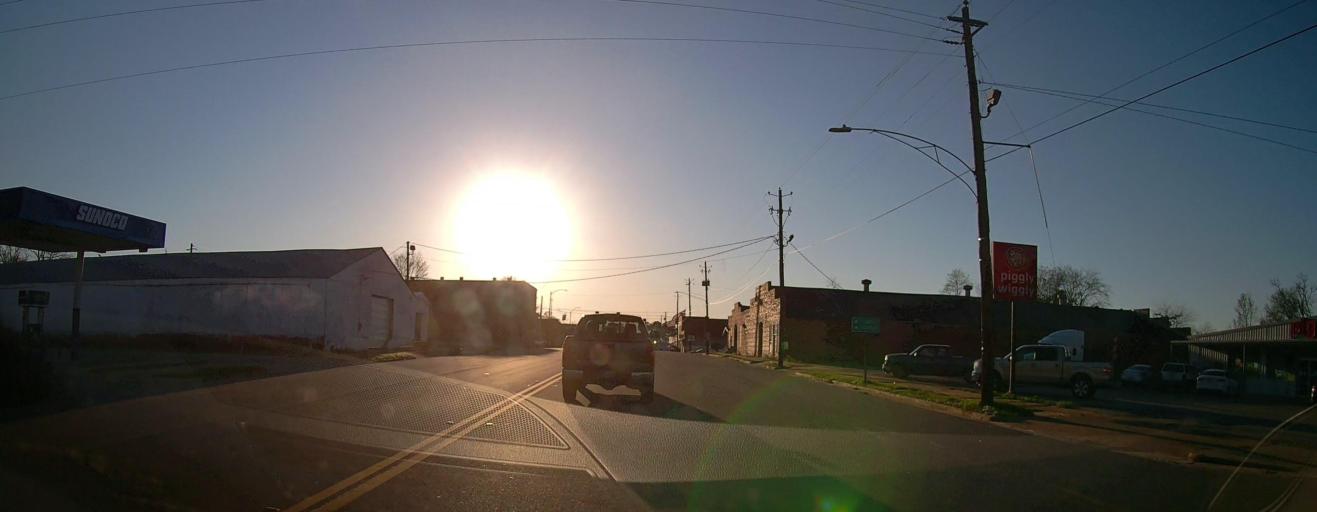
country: US
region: Georgia
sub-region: Wilcox County
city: Rochelle
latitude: 31.9509
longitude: -83.4531
